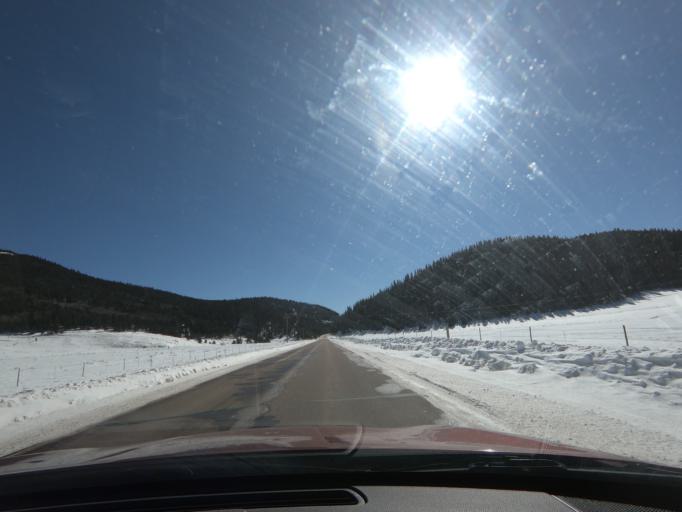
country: US
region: Colorado
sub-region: Teller County
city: Cripple Creek
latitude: 38.7571
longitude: -105.1073
